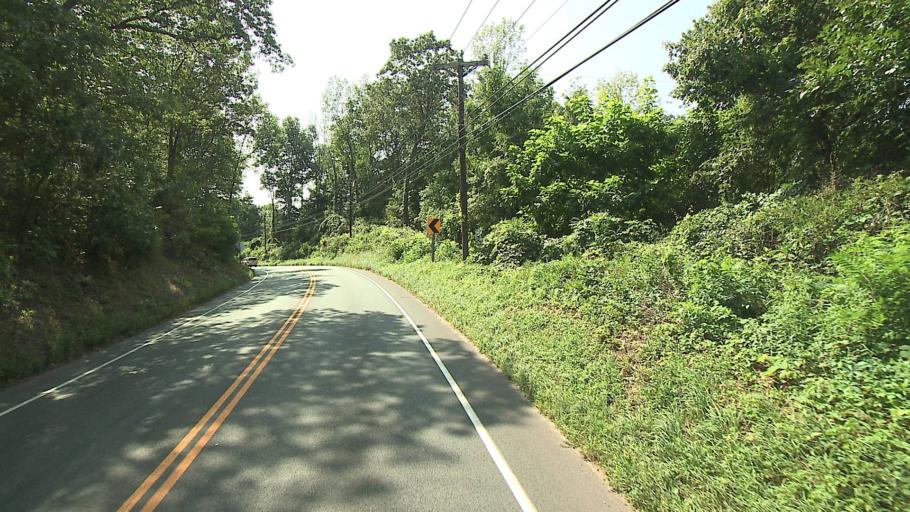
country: US
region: Connecticut
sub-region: Fairfield County
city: Newtown
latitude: 41.3576
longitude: -73.2641
